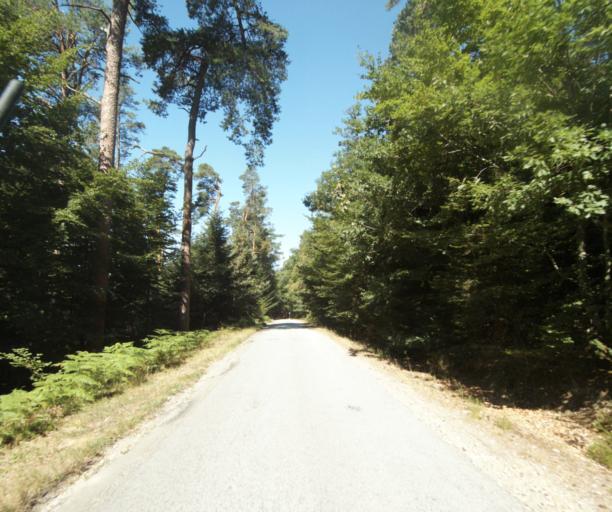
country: FR
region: Lorraine
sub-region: Departement des Vosges
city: Epinal
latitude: 48.1555
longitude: 6.4677
